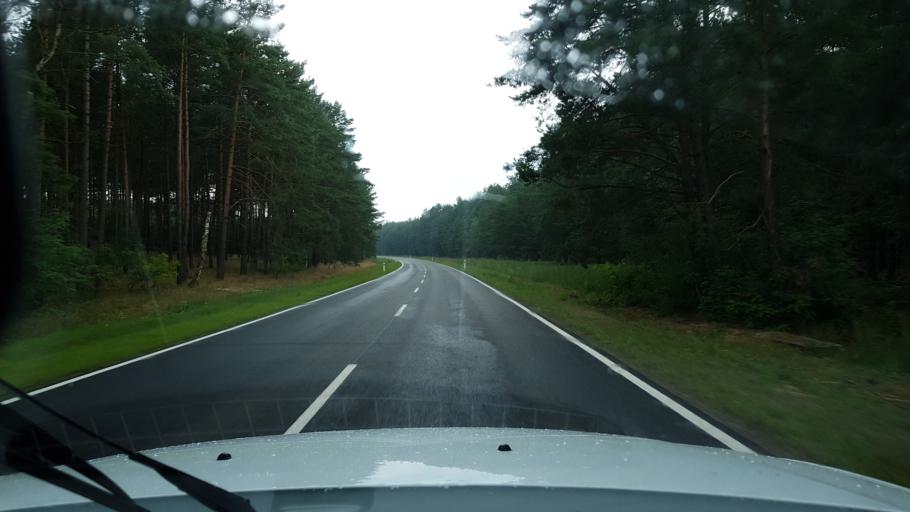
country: PL
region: West Pomeranian Voivodeship
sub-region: Powiat goleniowski
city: Mosty
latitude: 53.4418
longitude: 14.9310
